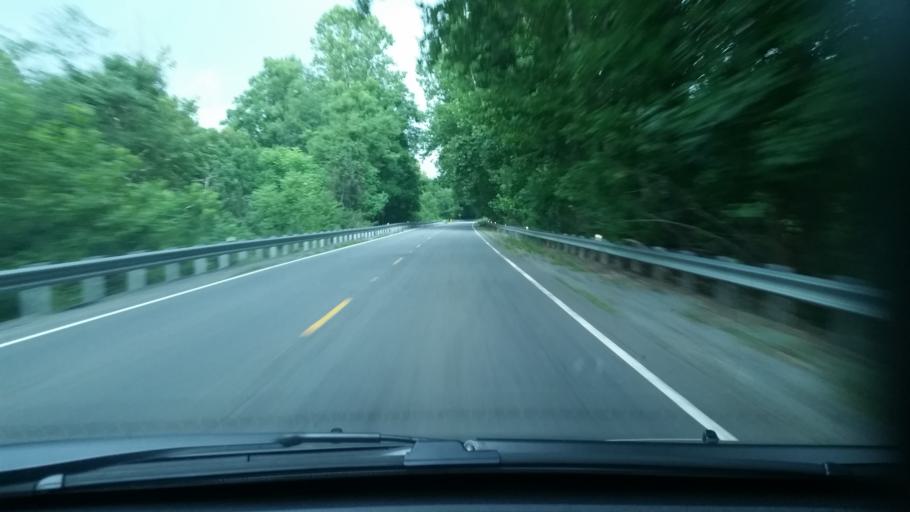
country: US
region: Virginia
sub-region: Nelson County
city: Nellysford
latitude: 37.9032
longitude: -78.8324
